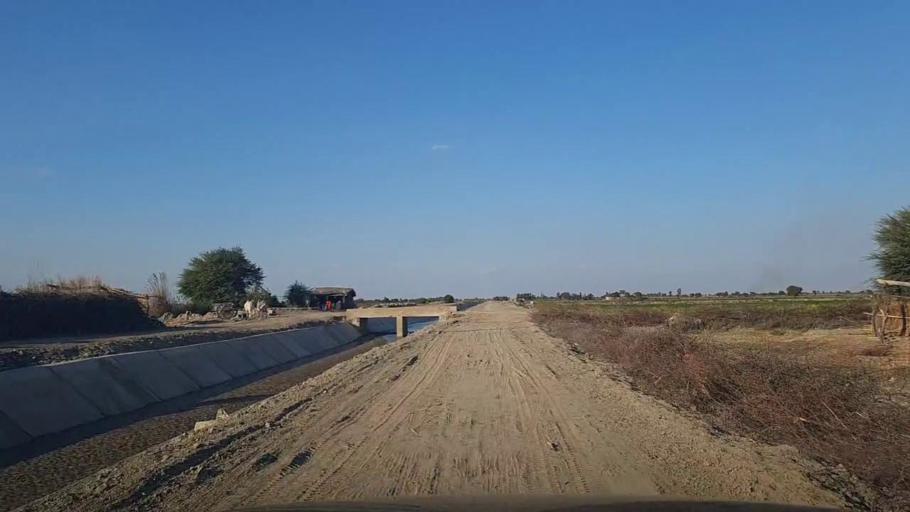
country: PK
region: Sindh
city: Jhol
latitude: 25.9188
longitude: 69.0410
